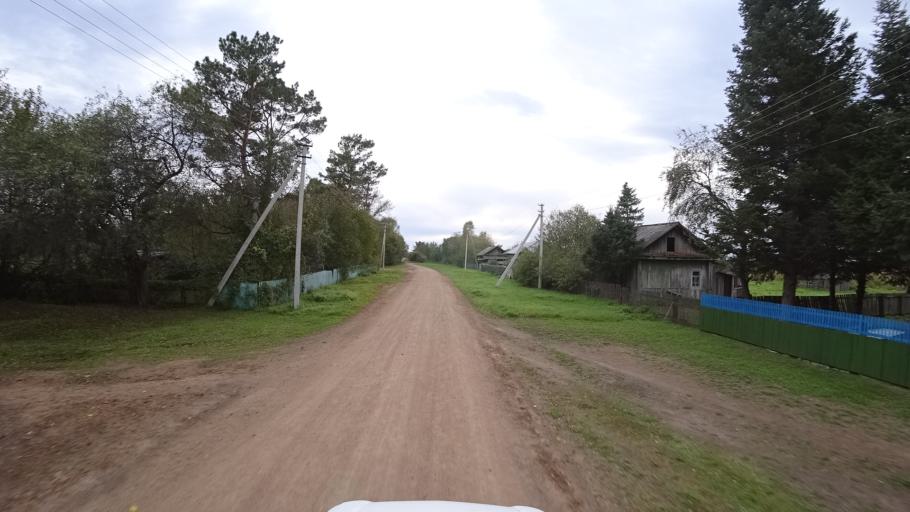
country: RU
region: Amur
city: Arkhara
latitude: 49.4354
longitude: 130.2677
